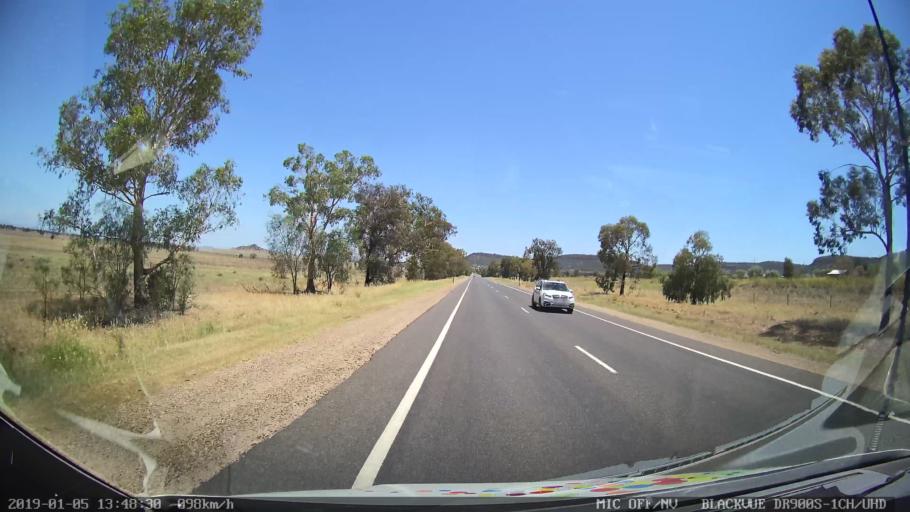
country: AU
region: New South Wales
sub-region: Gunnedah
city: Gunnedah
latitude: -31.0026
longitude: 150.2777
